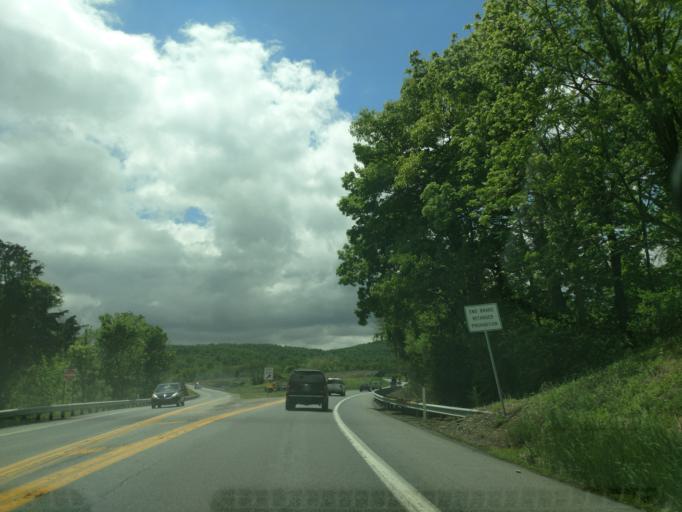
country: US
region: Pennsylvania
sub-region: Lebanon County
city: Cornwall
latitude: 40.2735
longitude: -76.4367
